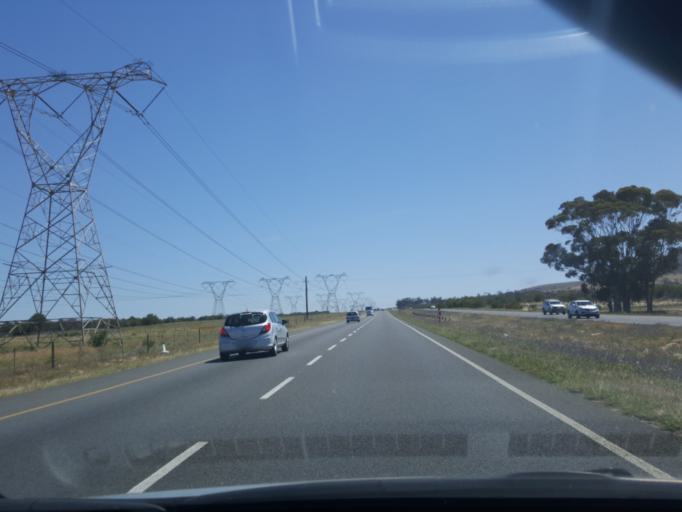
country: ZA
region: Western Cape
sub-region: City of Cape Town
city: Sunset Beach
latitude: -33.7443
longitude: 18.5458
